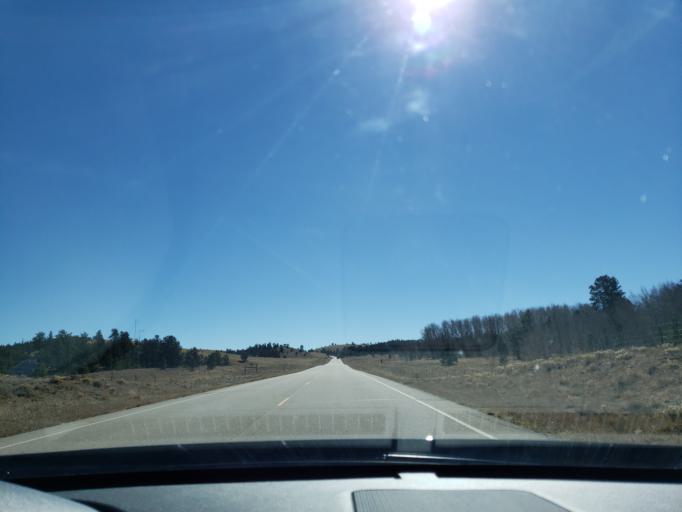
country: US
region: Colorado
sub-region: Chaffee County
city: Buena Vista
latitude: 38.9035
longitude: -105.6964
